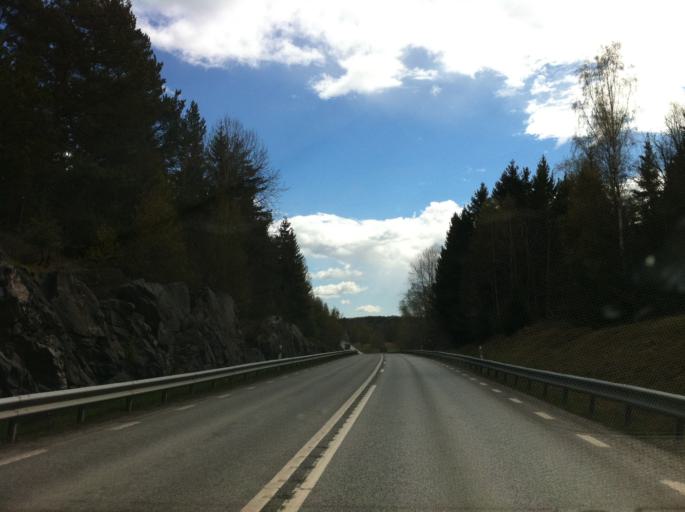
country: SE
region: Stockholm
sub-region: Vallentuna Kommun
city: Vallentuna
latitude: 59.4867
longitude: 18.1652
